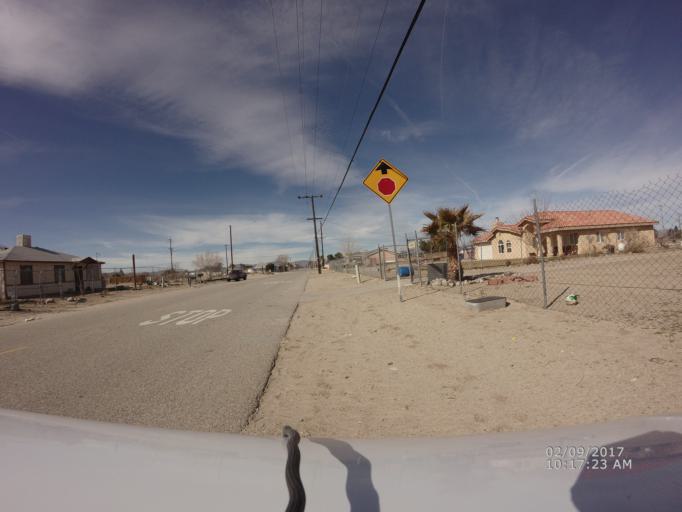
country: US
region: California
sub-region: Los Angeles County
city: Littlerock
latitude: 34.5727
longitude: -117.9330
